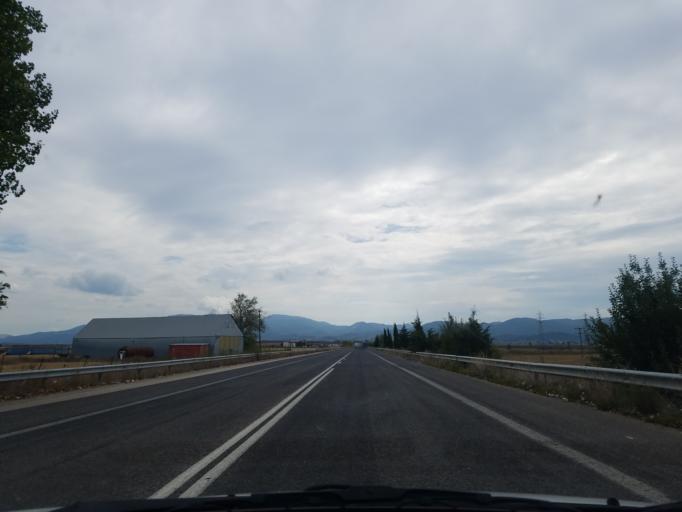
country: GR
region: Central Greece
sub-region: Nomos Fthiotidos
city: Omvriaki
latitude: 39.0732
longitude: 22.3194
